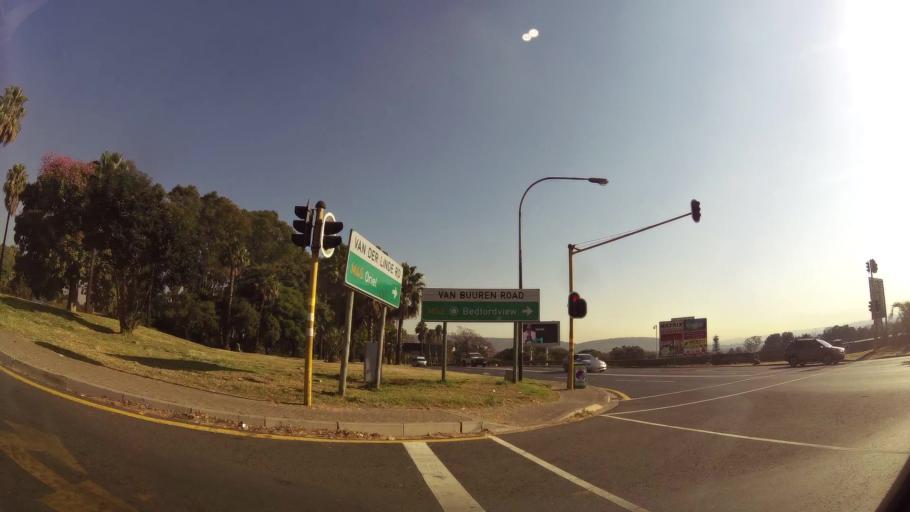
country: ZA
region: Gauteng
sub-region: Ekurhuleni Metropolitan Municipality
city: Germiston
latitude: -26.1945
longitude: 28.1302
